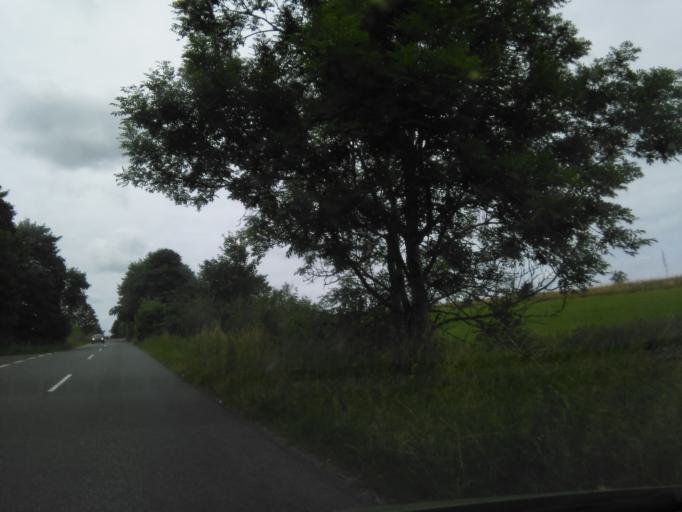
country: DK
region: Central Jutland
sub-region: Arhus Kommune
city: Solbjerg
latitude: 56.0329
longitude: 10.0697
